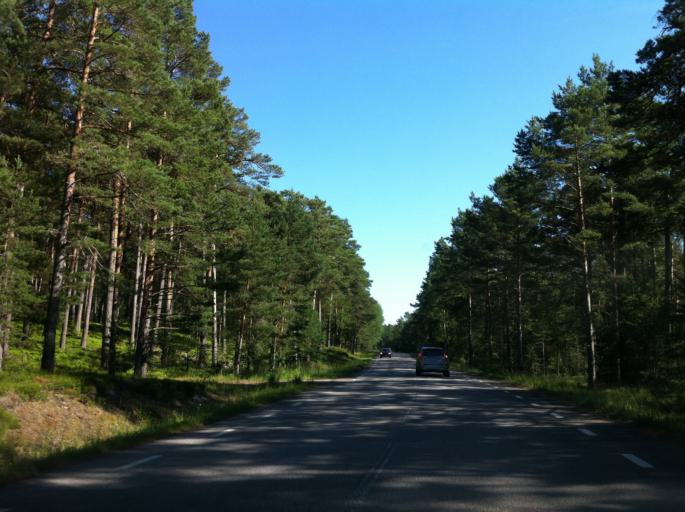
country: SE
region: Kalmar
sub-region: Borgholms Kommun
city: Borgholm
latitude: 57.3039
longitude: 17.0244
